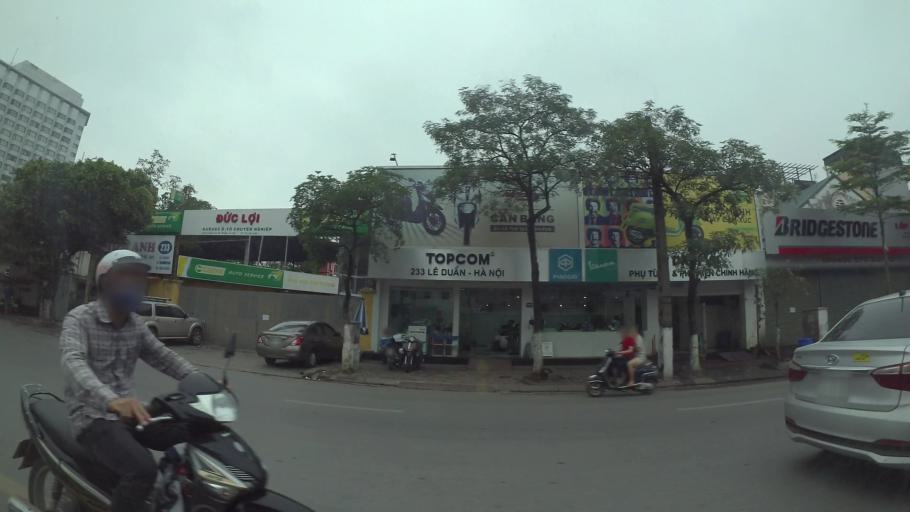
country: VN
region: Ha Noi
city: Hai BaTrung
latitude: 21.0167
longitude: 105.8414
